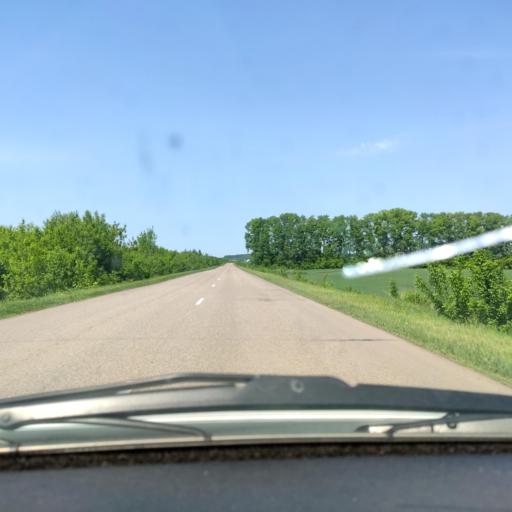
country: RU
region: Bashkortostan
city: Avdon
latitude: 54.5354
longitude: 55.6434
